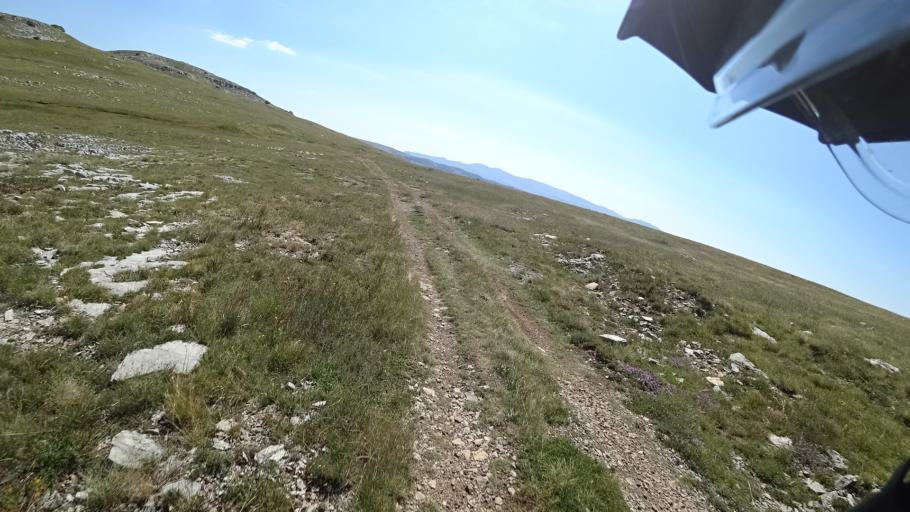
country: HR
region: Splitsko-Dalmatinska
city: Hrvace
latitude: 43.9030
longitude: 16.6068
